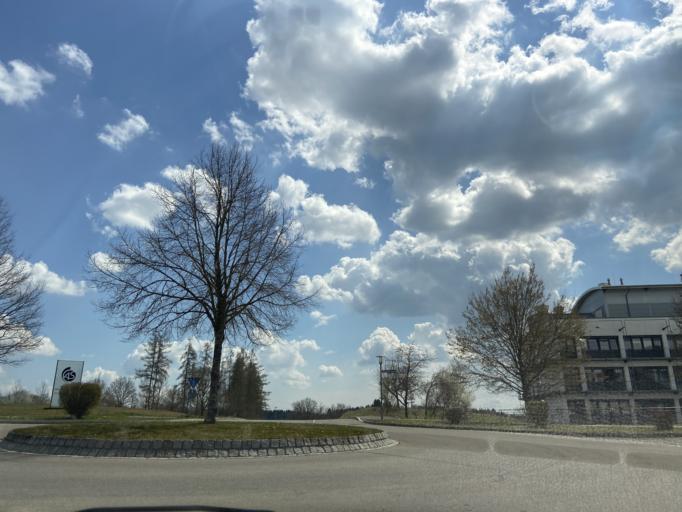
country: DE
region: Baden-Wuerttemberg
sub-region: Tuebingen Region
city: Sigmaringen
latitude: 48.0870
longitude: 9.2378
